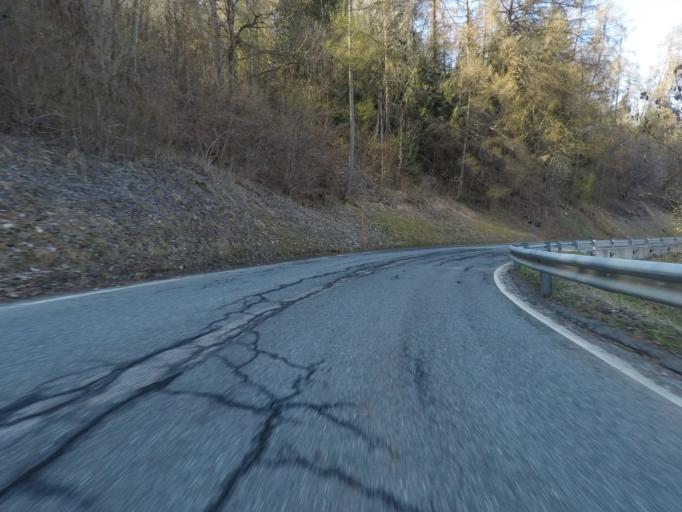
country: CH
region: Valais
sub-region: Conthey District
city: Basse-Nendaz
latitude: 46.1860
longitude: 7.3298
